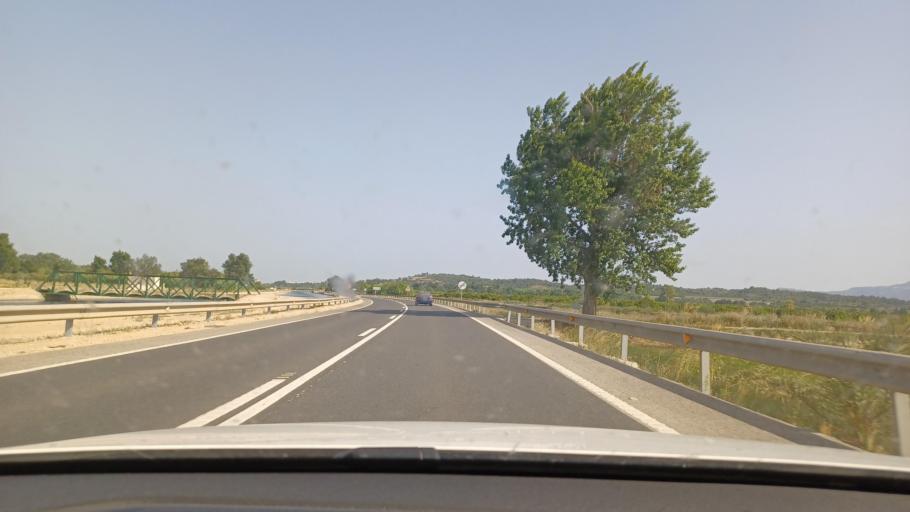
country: ES
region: Catalonia
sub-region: Provincia de Tarragona
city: Masdenverge
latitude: 40.7564
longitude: 0.5384
